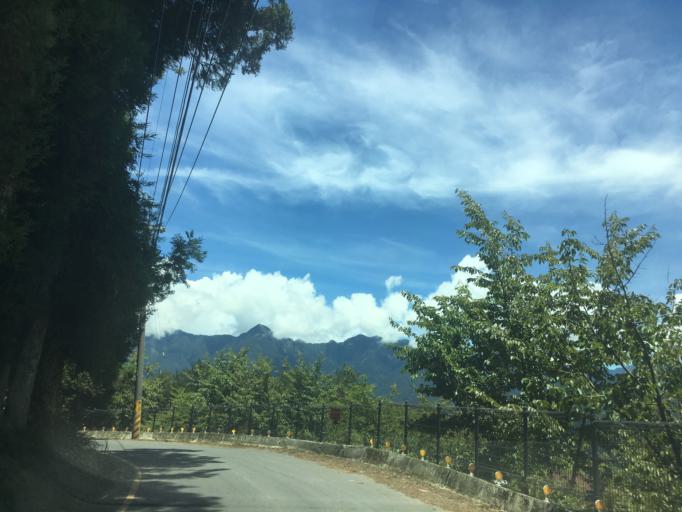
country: TW
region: Taiwan
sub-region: Nantou
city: Puli
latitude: 24.2501
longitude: 121.2478
